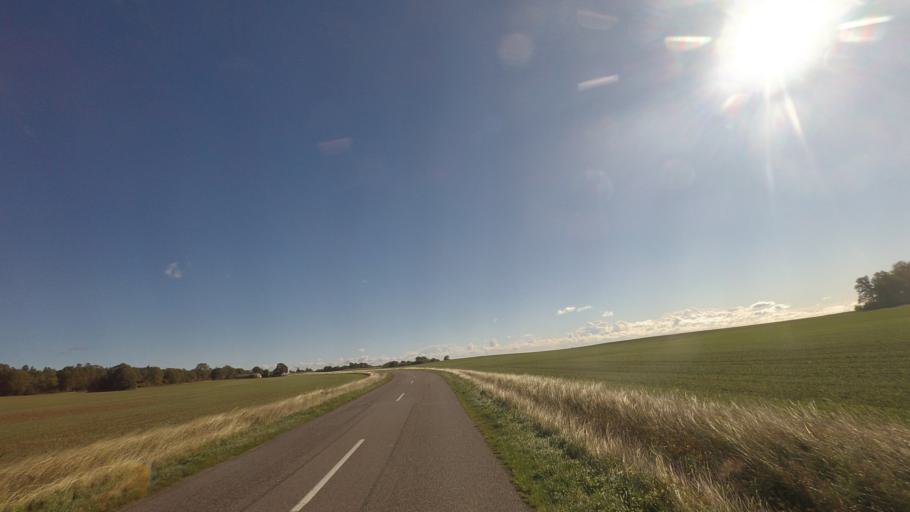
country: DK
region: Capital Region
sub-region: Bornholm Kommune
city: Nexo
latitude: 55.0774
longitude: 15.0863
